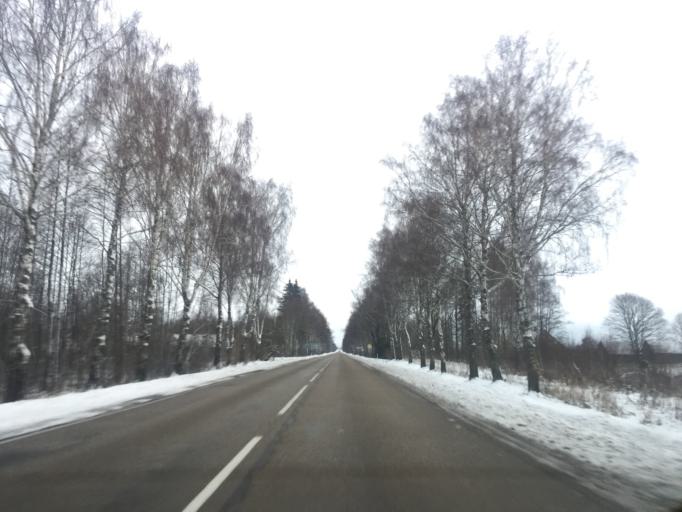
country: LV
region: Karsava
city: Karsava
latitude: 56.7821
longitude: 27.6998
